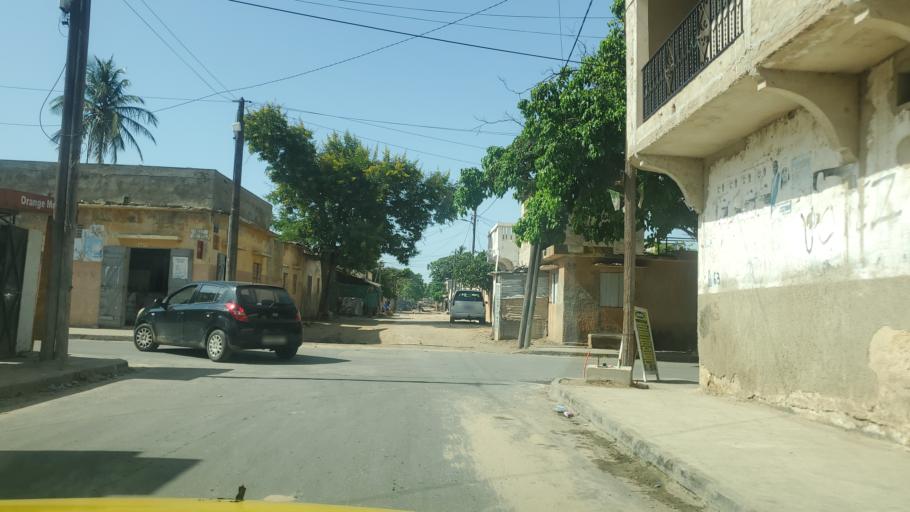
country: SN
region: Saint-Louis
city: Saint-Louis
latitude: 16.0214
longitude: -16.4858
